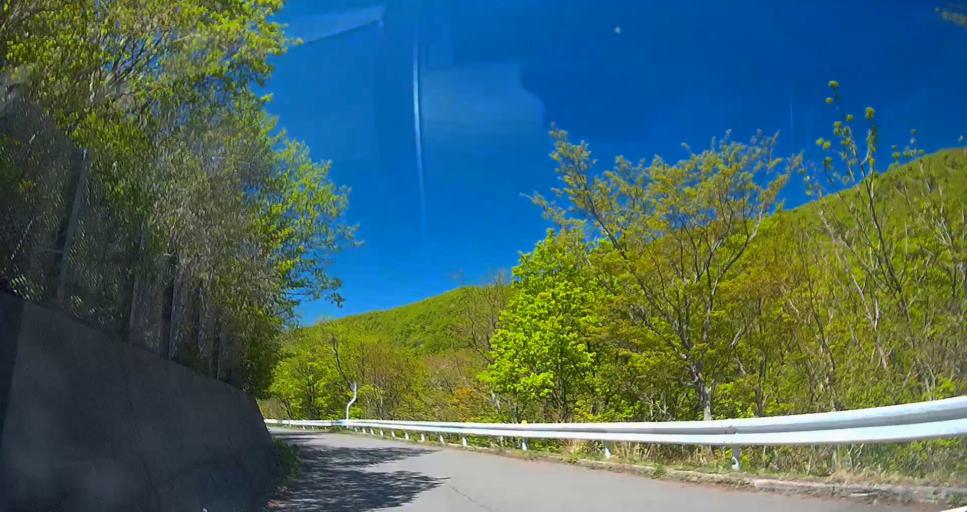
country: JP
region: Aomori
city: Mutsu
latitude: 41.3244
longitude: 140.8171
